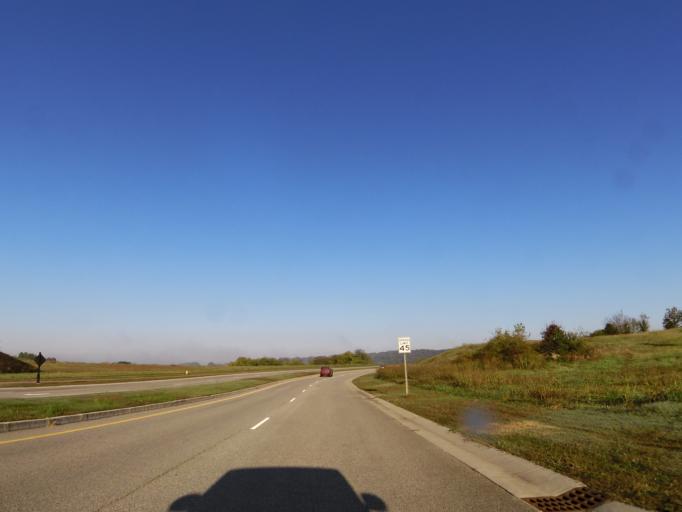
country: US
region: Tennessee
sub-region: Blount County
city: Eagleton Village
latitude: 35.8040
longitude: -83.9422
